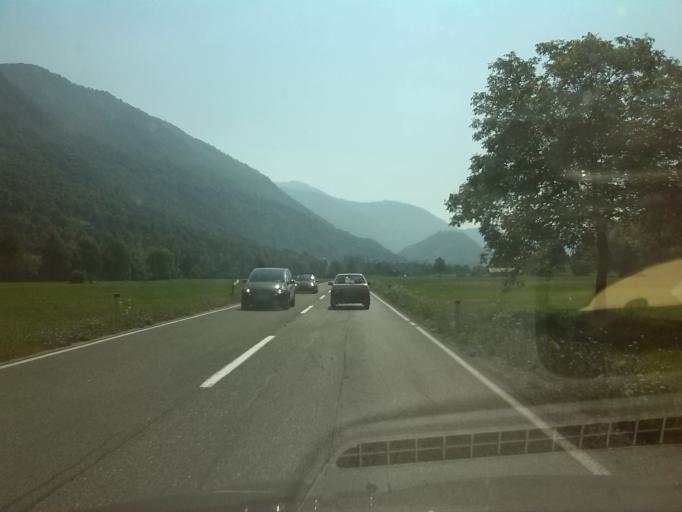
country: SI
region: Tolmin
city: Tolmin
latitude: 46.2042
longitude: 13.6761
